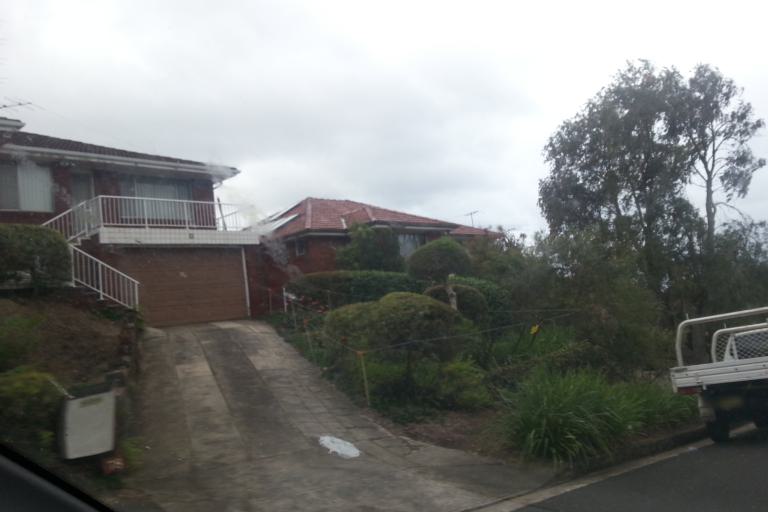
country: AU
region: New South Wales
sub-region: Wollongong
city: Keiraville
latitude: -34.4105
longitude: 150.8667
